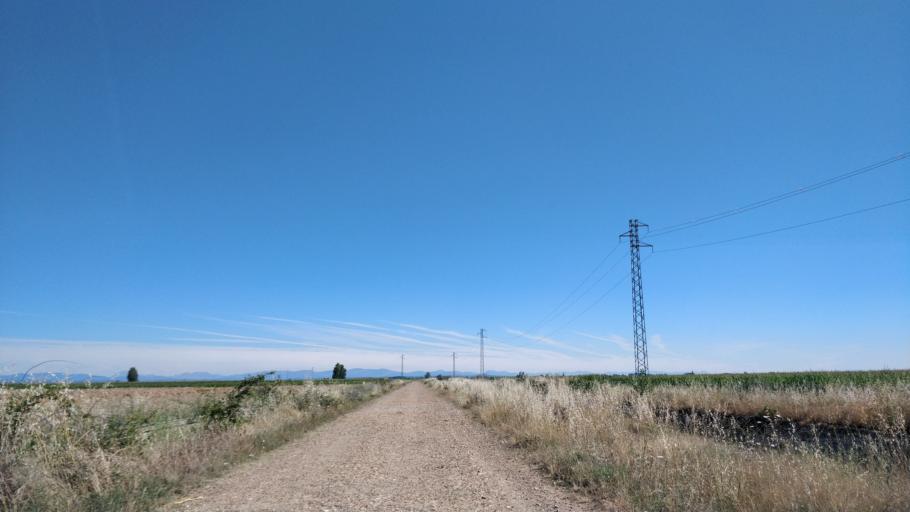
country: ES
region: Castille and Leon
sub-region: Provincia de Leon
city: Bustillo del Paramo
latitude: 42.4343
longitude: -5.8217
